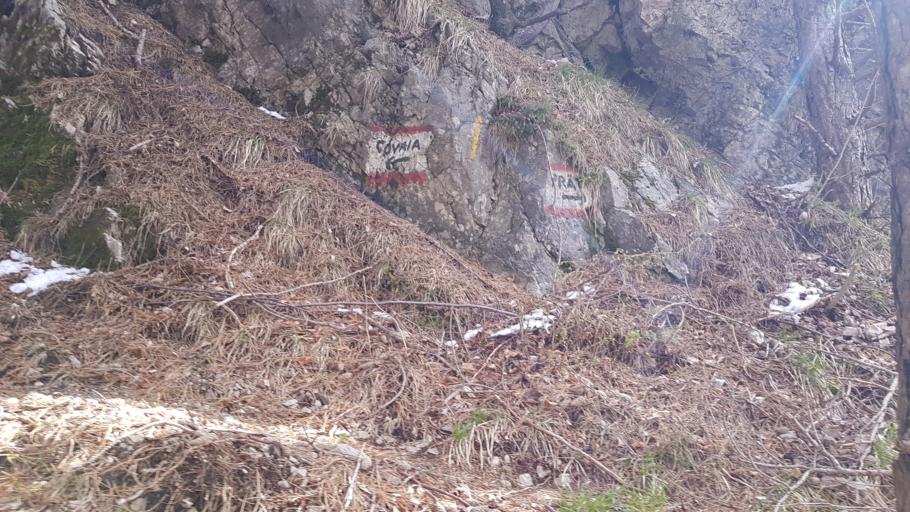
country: IT
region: Friuli Venezia Giulia
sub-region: Provincia di Udine
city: Trasaghis
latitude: 46.2730
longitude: 13.0170
